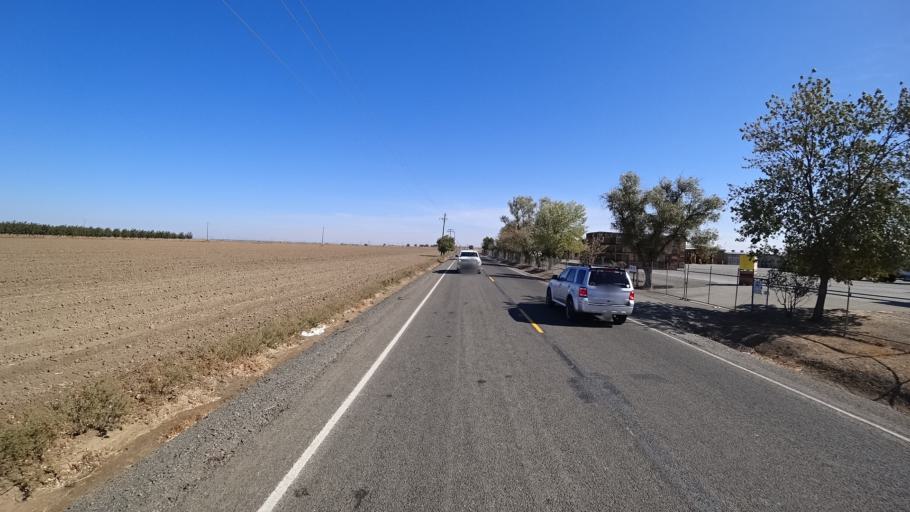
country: US
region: California
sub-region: Yolo County
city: Cottonwood
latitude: 38.6204
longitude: -121.9649
